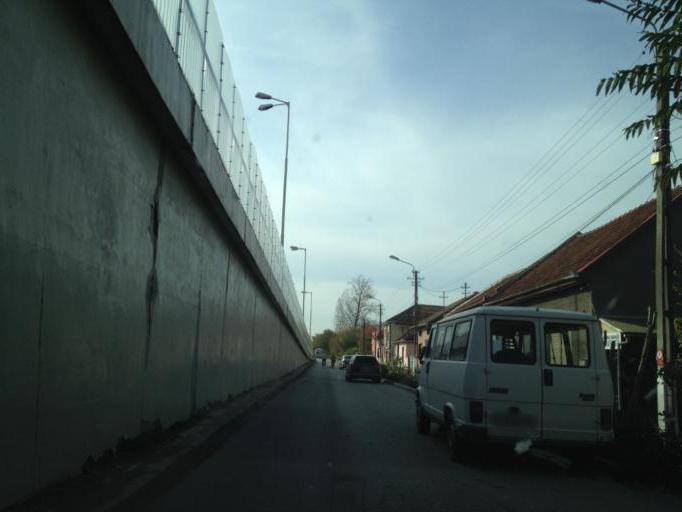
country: RO
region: Timis
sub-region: Municipiul Lugoj
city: Lugoj
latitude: 45.6854
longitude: 21.8856
